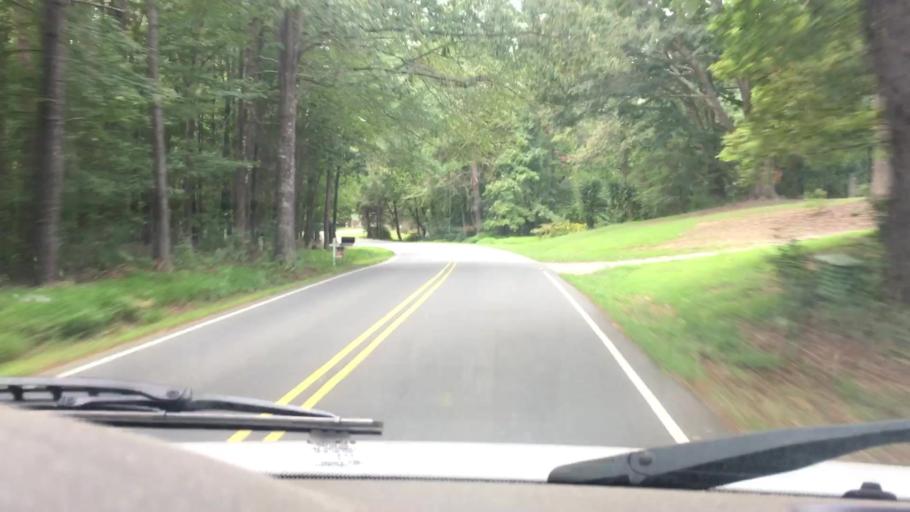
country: US
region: North Carolina
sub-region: Gaston County
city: Davidson
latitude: 35.4997
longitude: -80.8309
